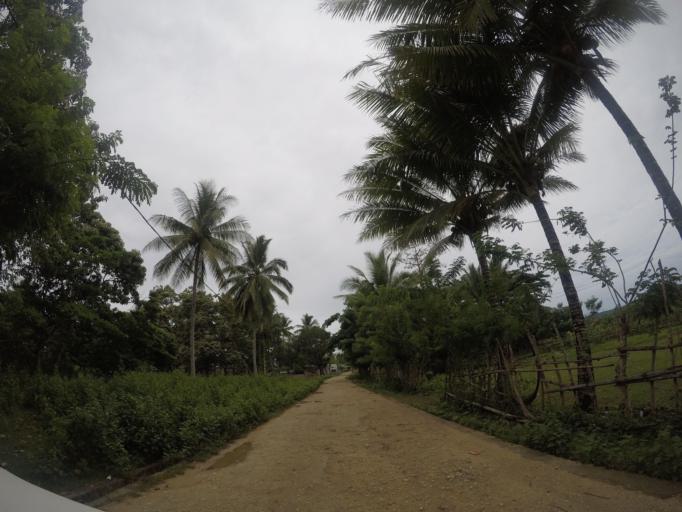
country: TL
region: Lautem
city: Lospalos
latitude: -8.5215
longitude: 127.0033
